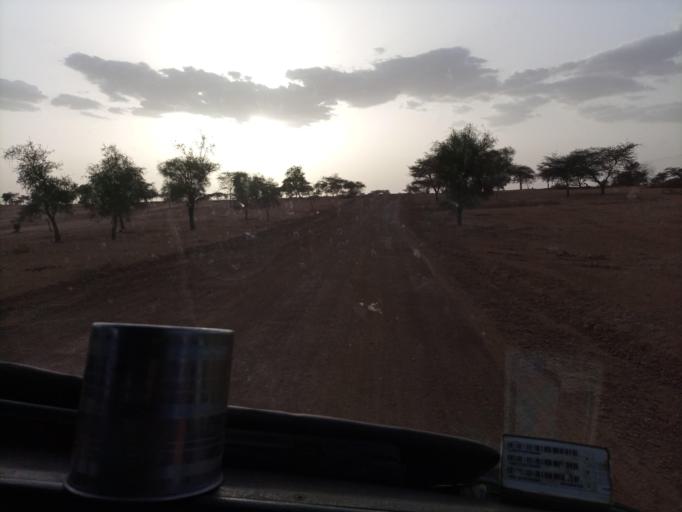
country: SN
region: Louga
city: Dara
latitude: 15.3737
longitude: -15.5854
